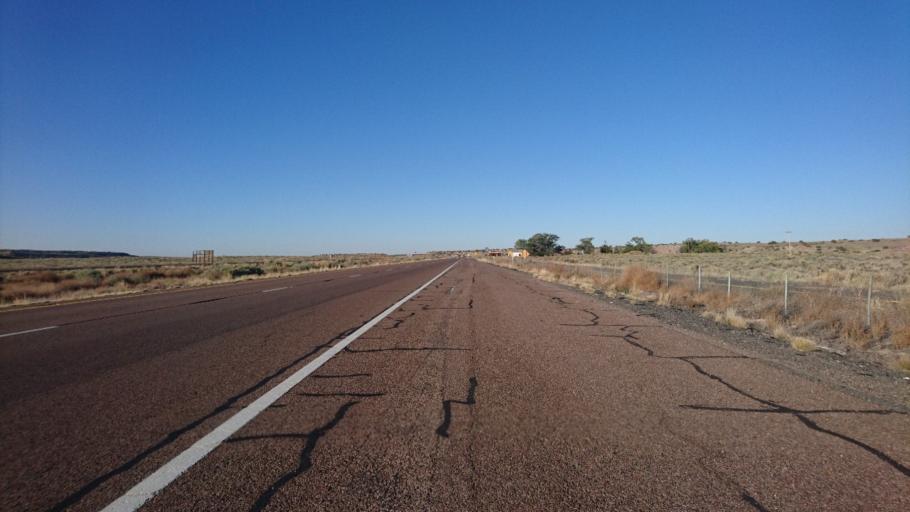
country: US
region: Arizona
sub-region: Apache County
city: Houck
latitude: 35.1893
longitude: -109.4407
